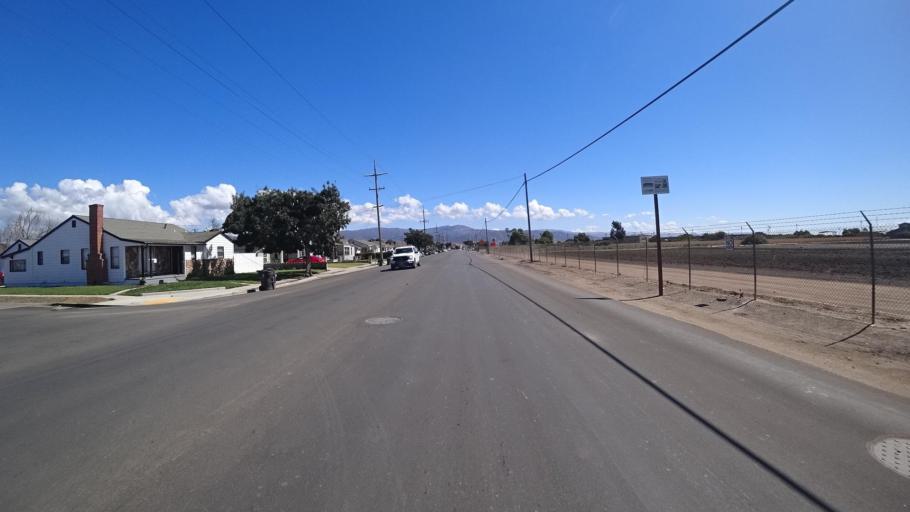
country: US
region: California
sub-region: Monterey County
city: Salinas
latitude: 36.6731
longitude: -121.6070
